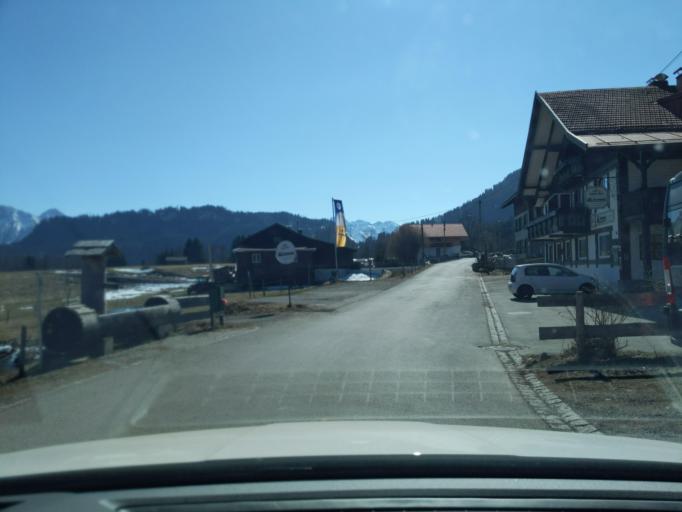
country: DE
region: Bavaria
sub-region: Swabia
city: Obermaiselstein
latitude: 47.4535
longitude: 10.2332
